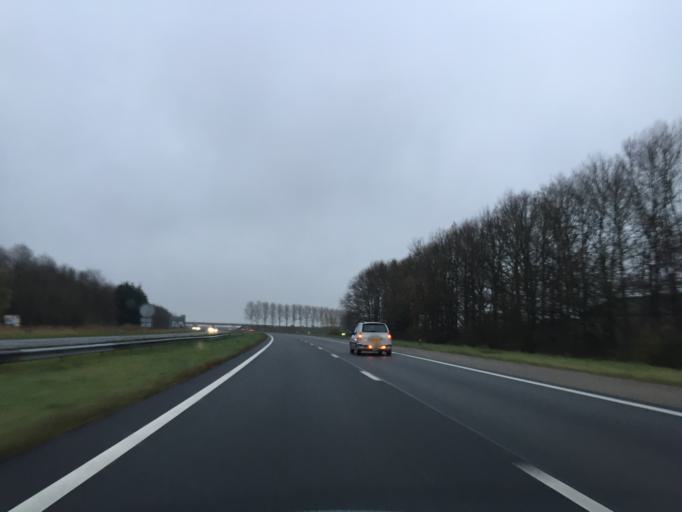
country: NL
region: Zeeland
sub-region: Gemeente Reimerswaal
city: Yerseke
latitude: 51.4574
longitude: 4.0317
